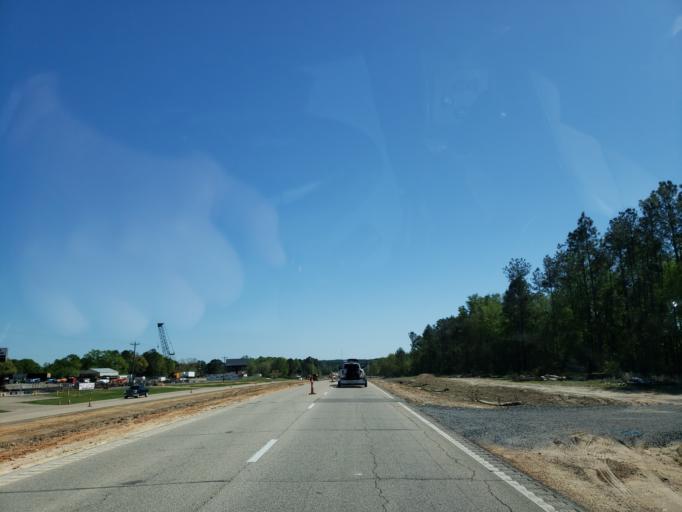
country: US
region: Mississippi
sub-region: Lamar County
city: Purvis
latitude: 31.0687
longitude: -89.2090
